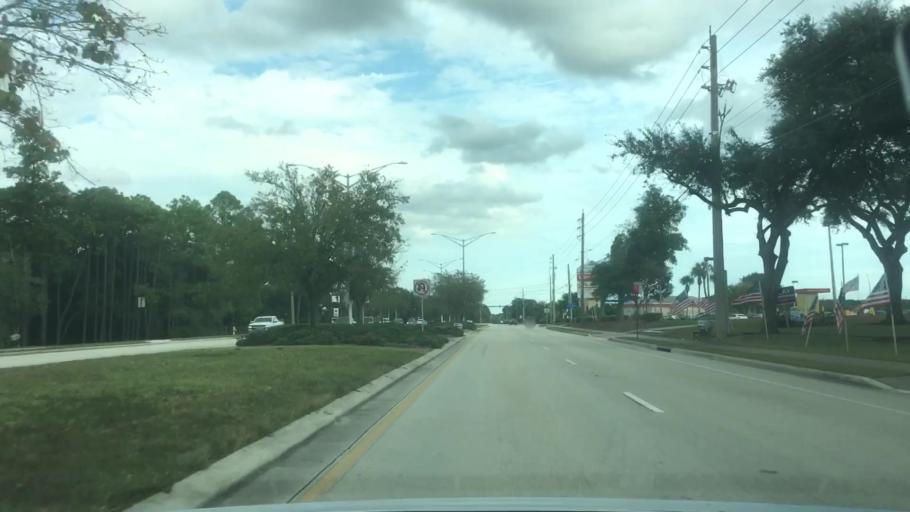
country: US
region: Florida
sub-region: Duval County
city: Atlantic Beach
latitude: 30.3468
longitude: -81.5264
